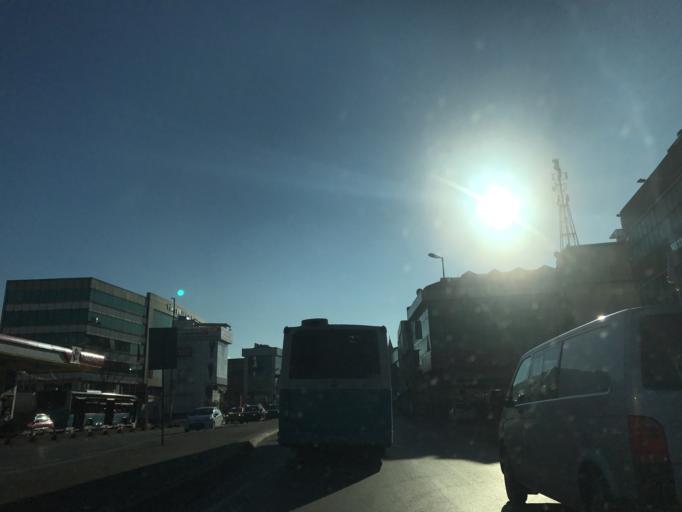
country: TR
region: Istanbul
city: Istanbul
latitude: 41.0418
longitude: 28.9193
